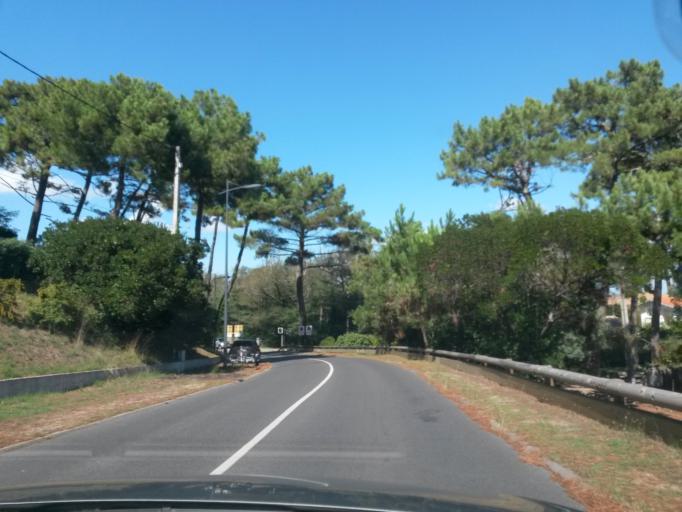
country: FR
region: Aquitaine
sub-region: Departement de la Gironde
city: Arcachon
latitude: 44.6708
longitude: -1.2407
